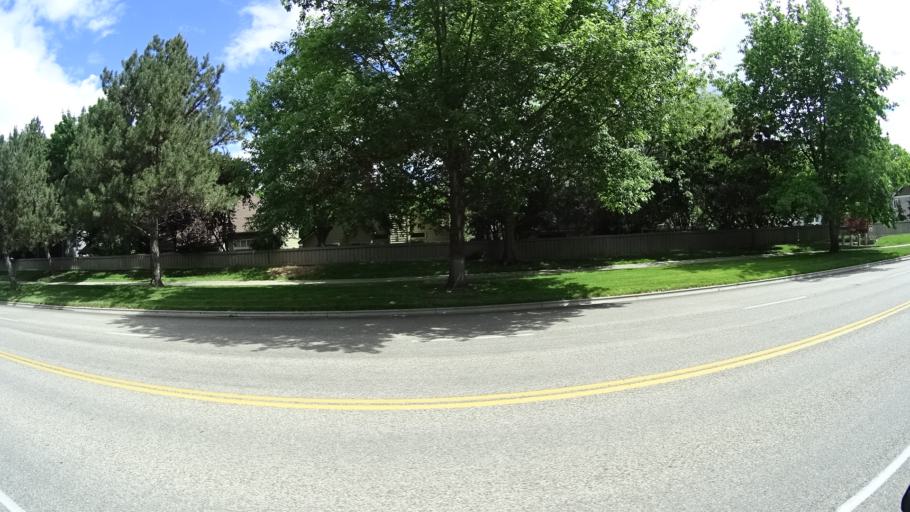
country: US
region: Idaho
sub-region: Ada County
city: Boise
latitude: 43.5792
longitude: -116.1600
